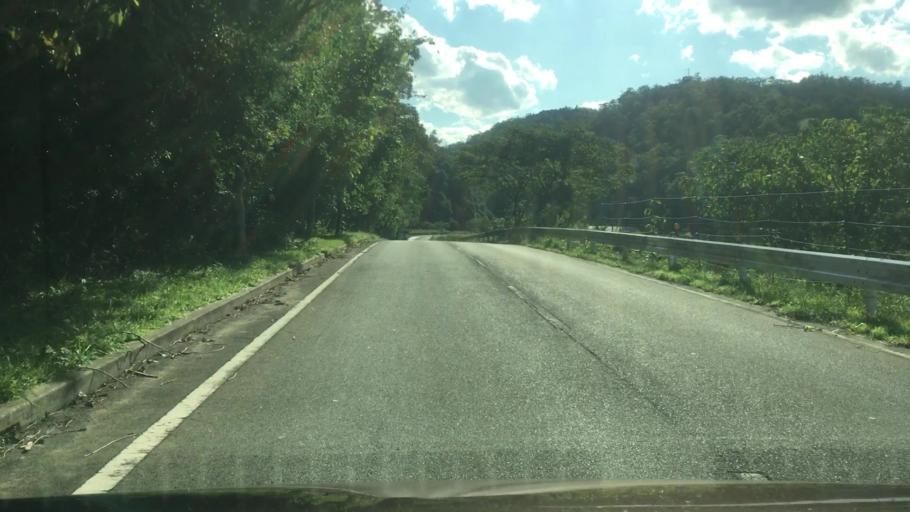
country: JP
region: Hyogo
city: Toyooka
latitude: 35.6458
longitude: 134.9633
